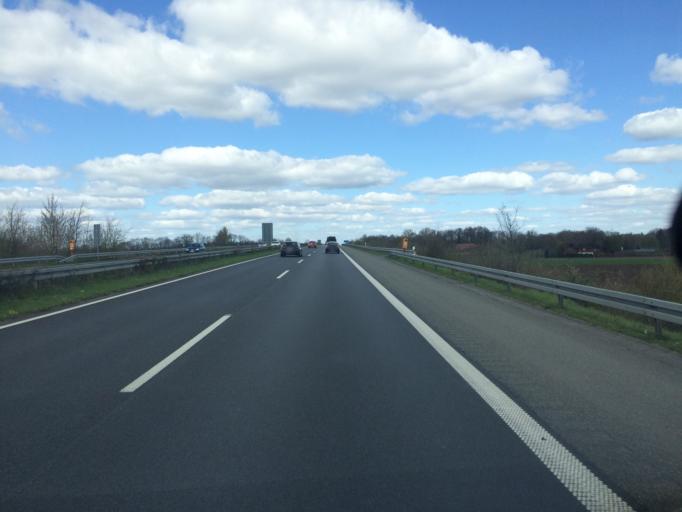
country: DE
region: North Rhine-Westphalia
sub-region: Regierungsbezirk Munster
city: Ochtrup
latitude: 52.2001
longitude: 7.1204
